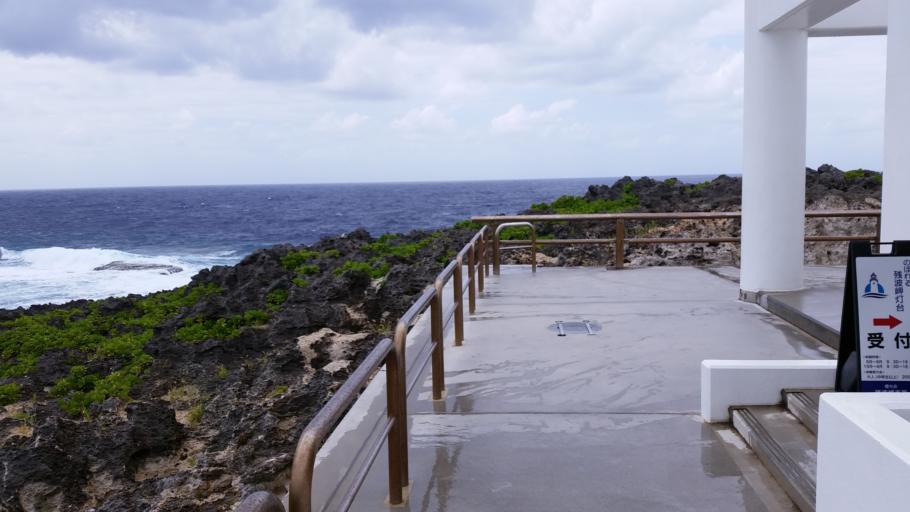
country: JP
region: Okinawa
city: Ishikawa
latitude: 26.4410
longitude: 127.7137
